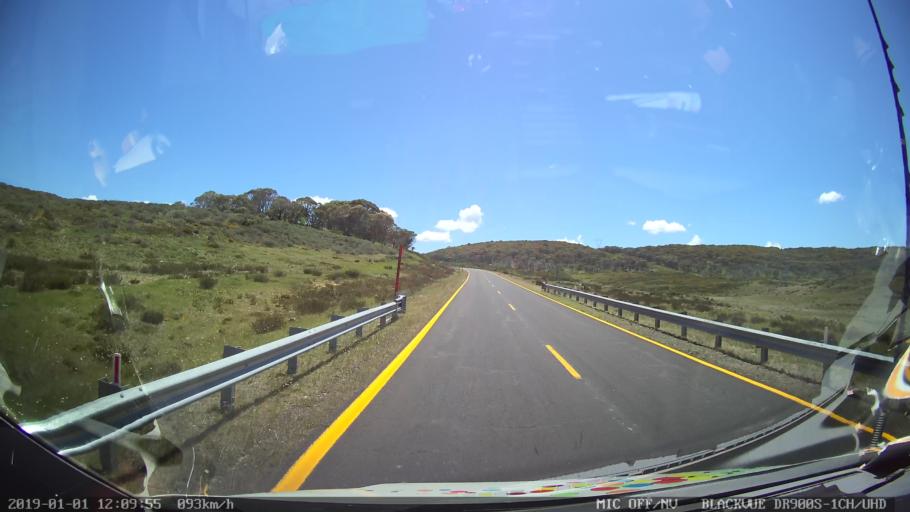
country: AU
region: New South Wales
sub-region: Tumut Shire
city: Tumut
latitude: -35.8014
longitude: 148.4973
